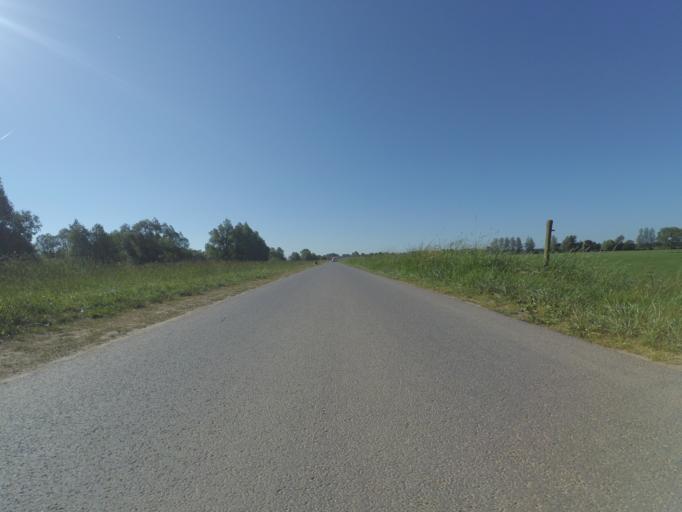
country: NL
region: Gelderland
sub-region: Gemeente Voorst
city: Wilp
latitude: 52.2282
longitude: 6.1613
